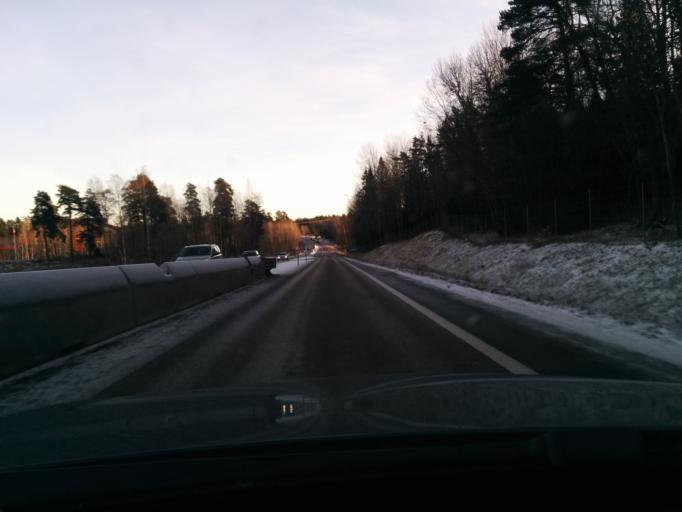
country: SE
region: Stockholm
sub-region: Jarfalla Kommun
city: Jakobsberg
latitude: 59.4771
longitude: 17.8497
